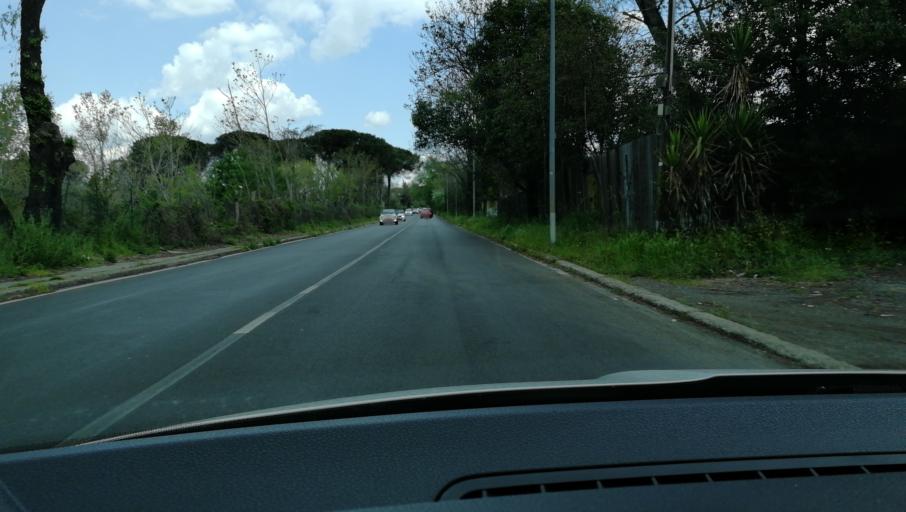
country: IT
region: Latium
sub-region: Citta metropolitana di Roma Capitale
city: Rome
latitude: 41.8561
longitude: 12.5314
